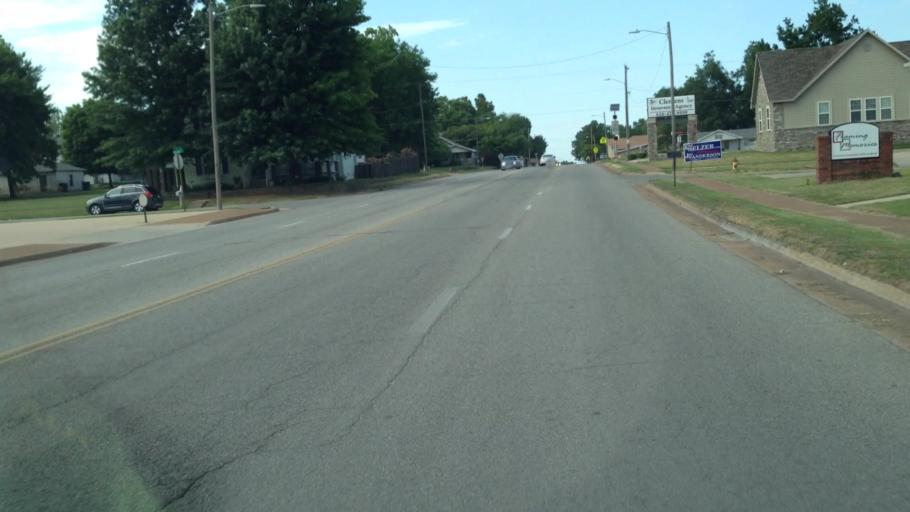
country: US
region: Kansas
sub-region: Labette County
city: Parsons
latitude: 37.3431
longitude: -95.2591
